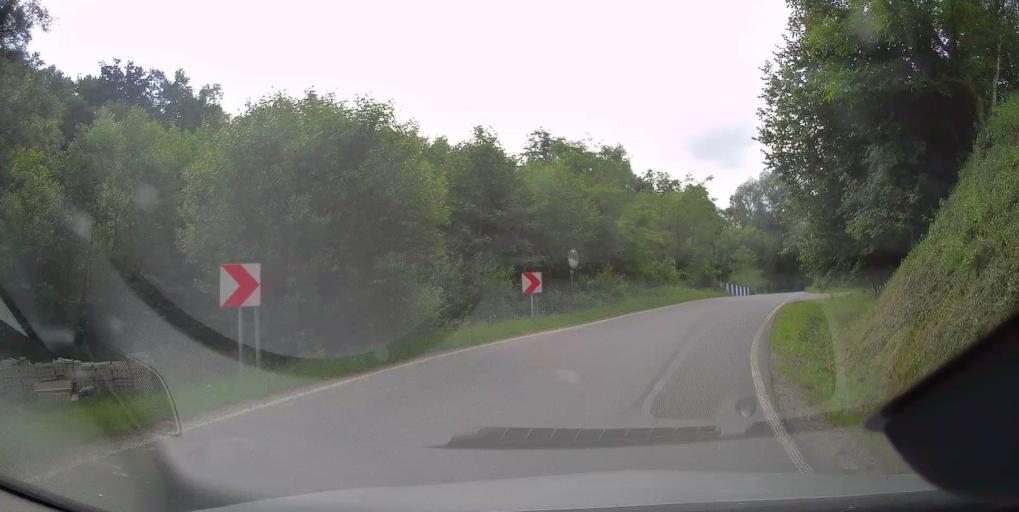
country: PL
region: Lesser Poland Voivodeship
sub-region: Powiat nowosadecki
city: Korzenna
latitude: 49.7242
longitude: 20.7747
